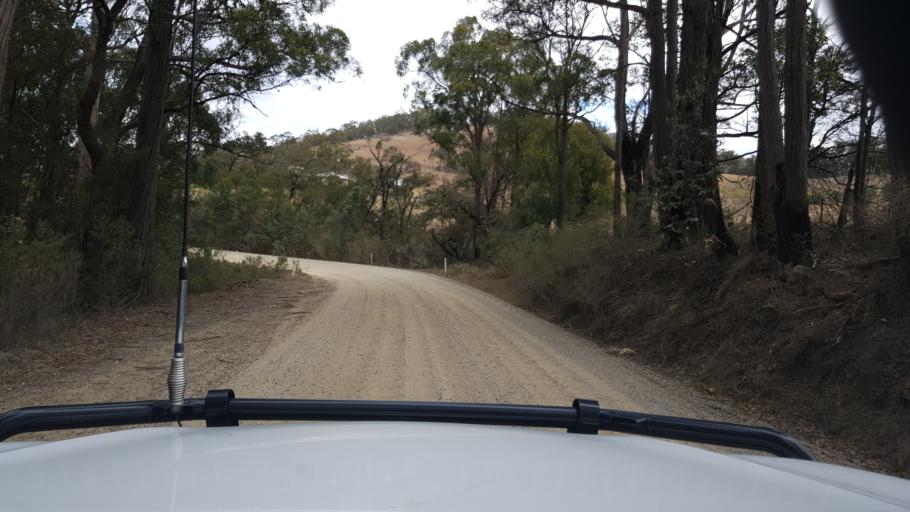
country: AU
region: Victoria
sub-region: East Gippsland
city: Bairnsdale
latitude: -37.6884
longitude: 147.5616
